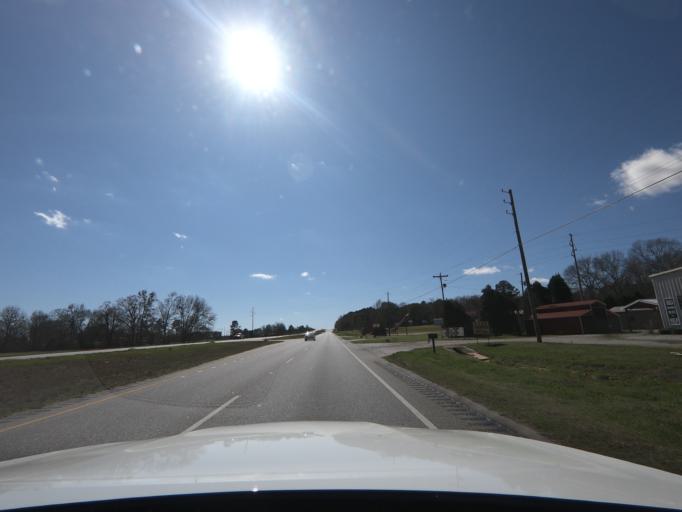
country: US
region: Alabama
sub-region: Barbour County
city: Eufaula
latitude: 31.7880
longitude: -85.1724
